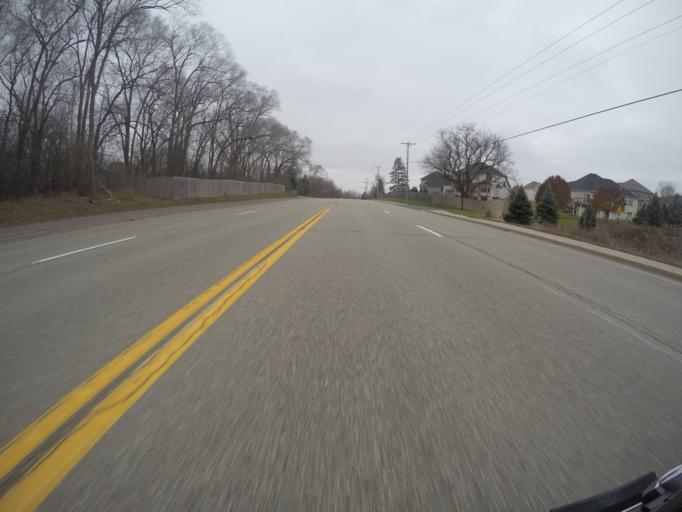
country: US
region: Minnesota
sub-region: Hennepin County
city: Eden Prairie
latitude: 44.8761
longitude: -93.4499
